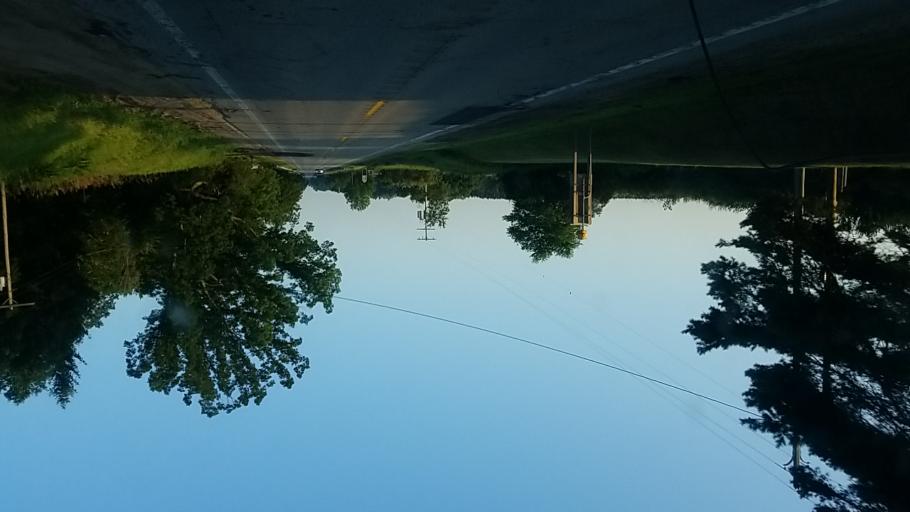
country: US
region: Michigan
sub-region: Isabella County
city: Lake Isabella
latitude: 43.6588
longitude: -85.1463
